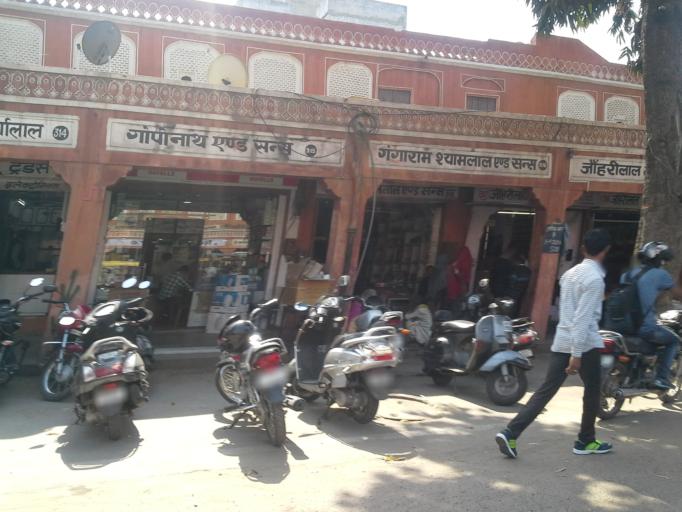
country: IN
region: Rajasthan
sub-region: Jaipur
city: Jaipur
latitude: 26.9240
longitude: 75.8215
